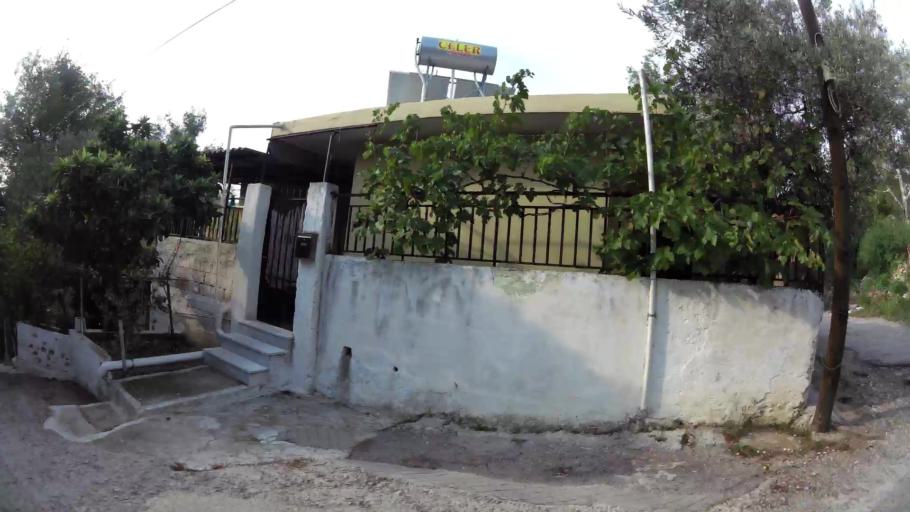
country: GR
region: Attica
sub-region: Nomarchia Athinas
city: Kamateron
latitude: 38.0610
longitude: 23.7016
